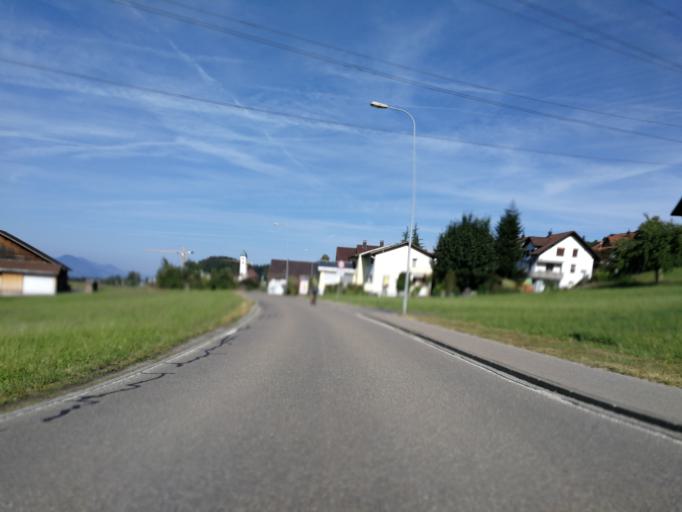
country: CH
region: Saint Gallen
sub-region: Wahlkreis See-Gaster
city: Gommiswald
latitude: 47.2376
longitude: 9.0106
